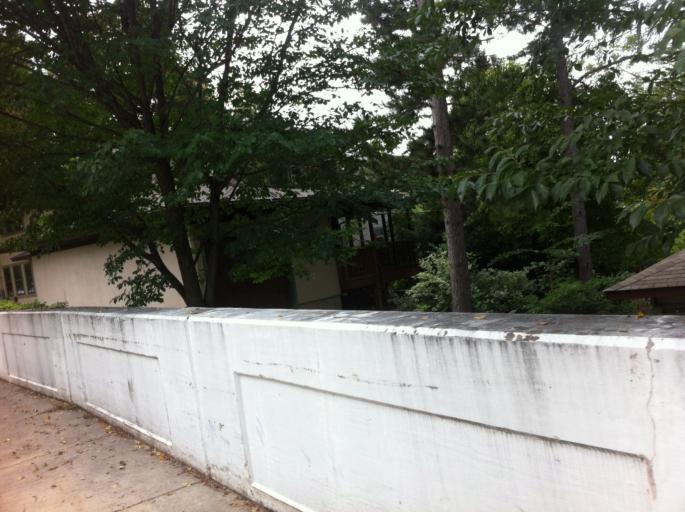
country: US
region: Wisconsin
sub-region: Dane County
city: Madison
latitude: 43.0649
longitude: -89.4239
